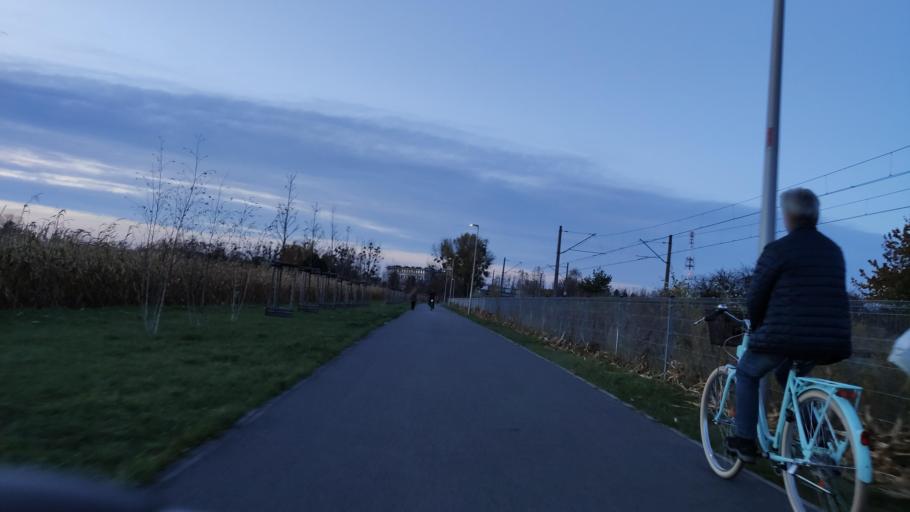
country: PL
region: Lower Silesian Voivodeship
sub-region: Powiat wroclawski
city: Zerniki Wroclawskie
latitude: 51.0660
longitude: 17.0657
